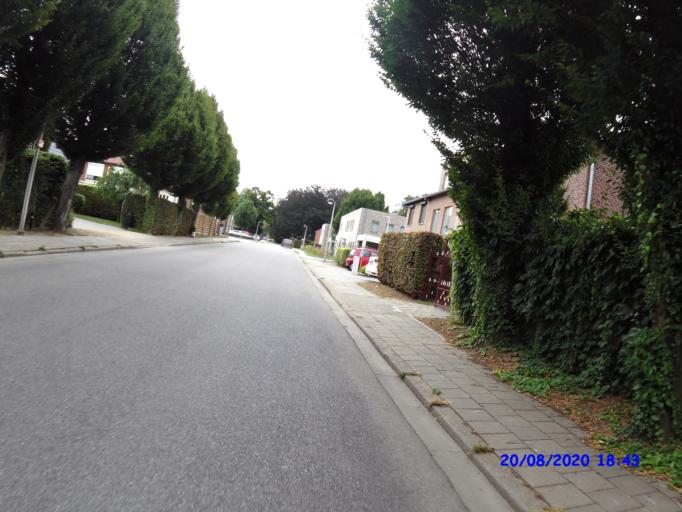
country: BE
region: Flanders
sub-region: Provincie Limburg
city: Sint-Truiden
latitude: 50.8253
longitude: 5.1779
